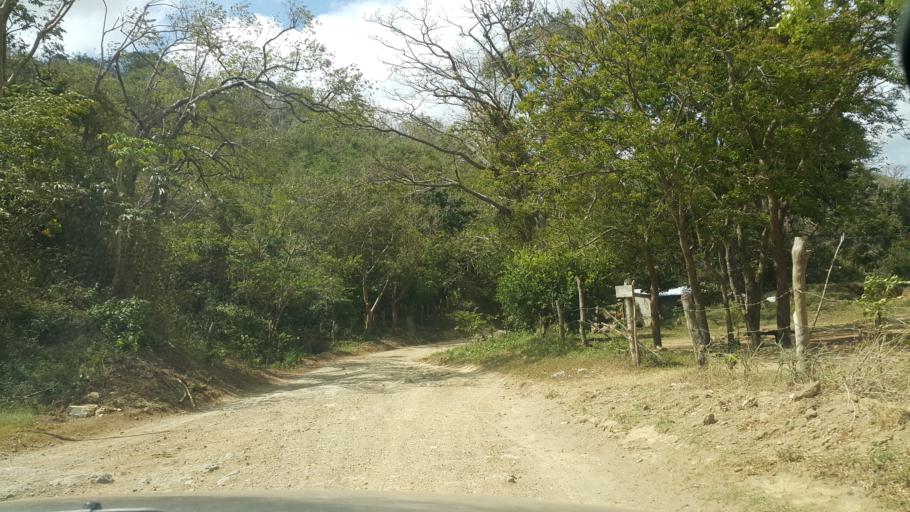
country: NI
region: Rivas
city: San Juan del Sur
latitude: 11.3014
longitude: -85.8598
